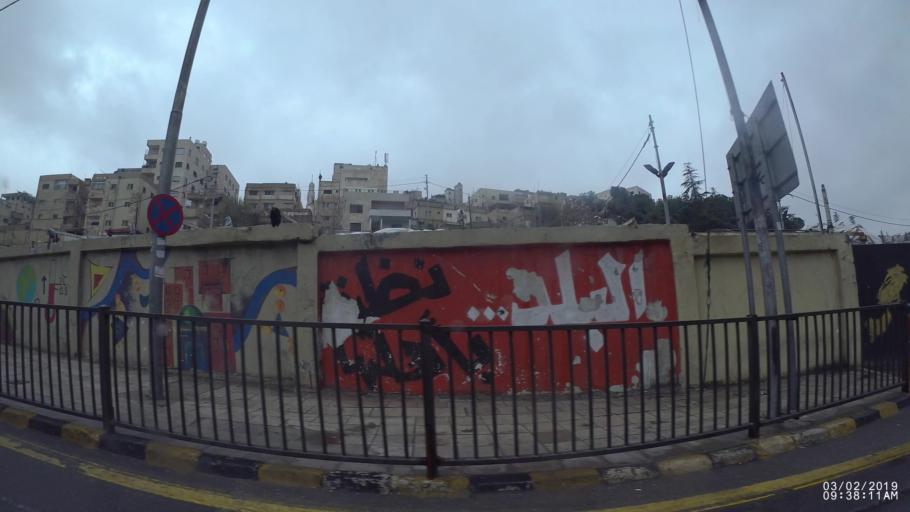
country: JO
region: Amman
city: Amman
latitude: 31.9472
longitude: 35.9158
